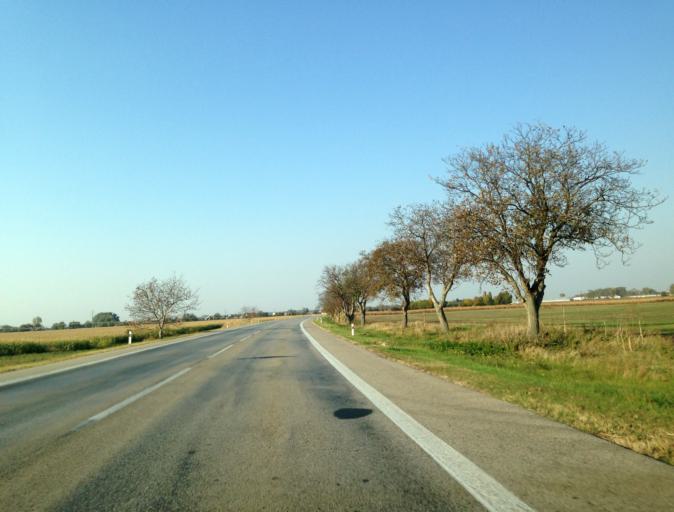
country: SK
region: Nitriansky
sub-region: Okres Komarno
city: Hurbanovo
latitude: 47.8327
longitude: 18.1720
